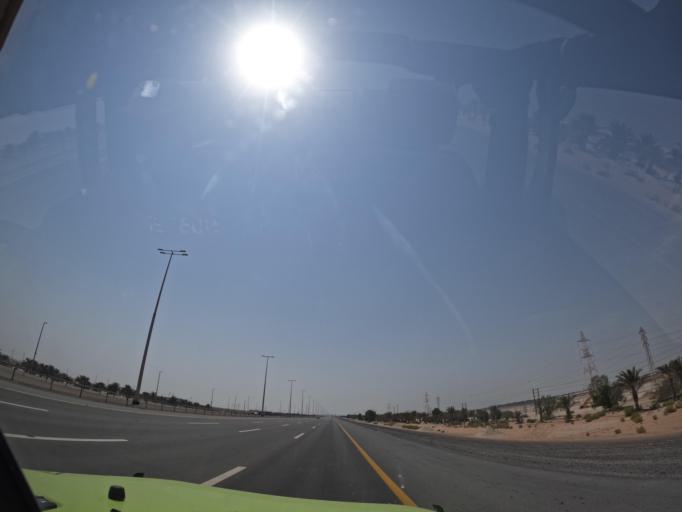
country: AE
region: Abu Dhabi
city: Abu Dhabi
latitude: 24.1867
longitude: 54.3809
